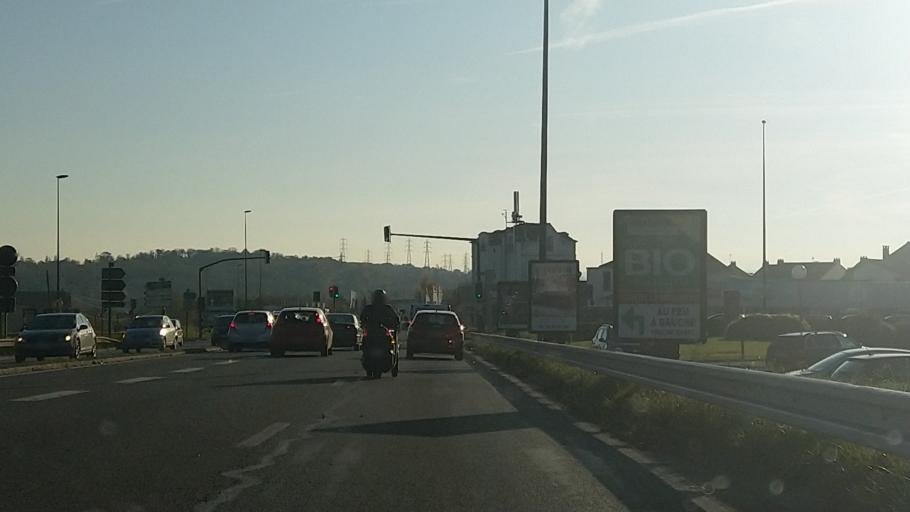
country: FR
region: Ile-de-France
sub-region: Departement du Val-d'Oise
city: Saint-Brice-sous-Foret
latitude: 48.9929
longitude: 2.3598
